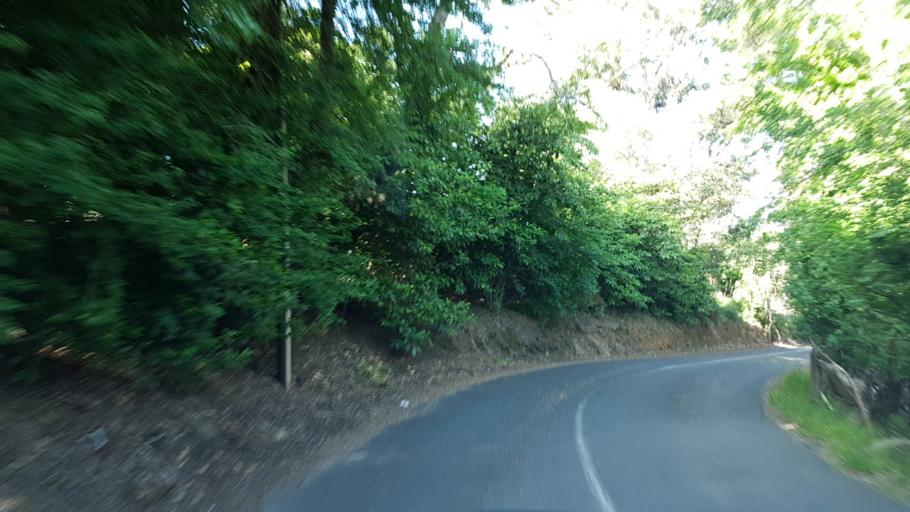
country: AU
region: South Australia
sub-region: Adelaide Hills
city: Adelaide Hills
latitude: -34.9112
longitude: 138.7664
